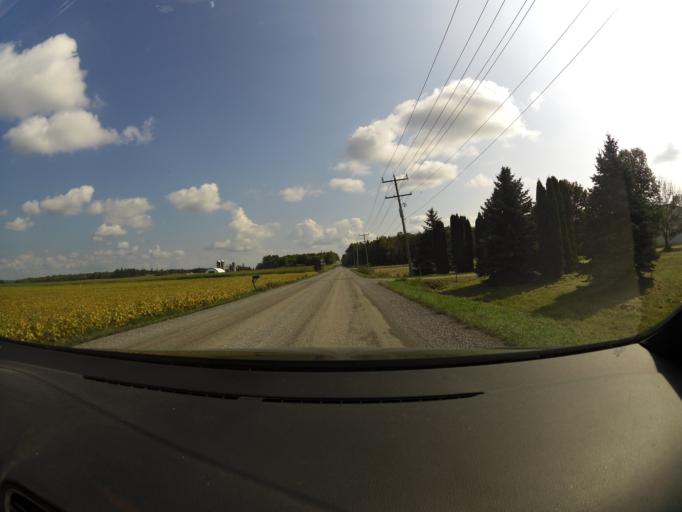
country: CA
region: Ontario
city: Arnprior
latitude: 45.4049
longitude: -76.2298
